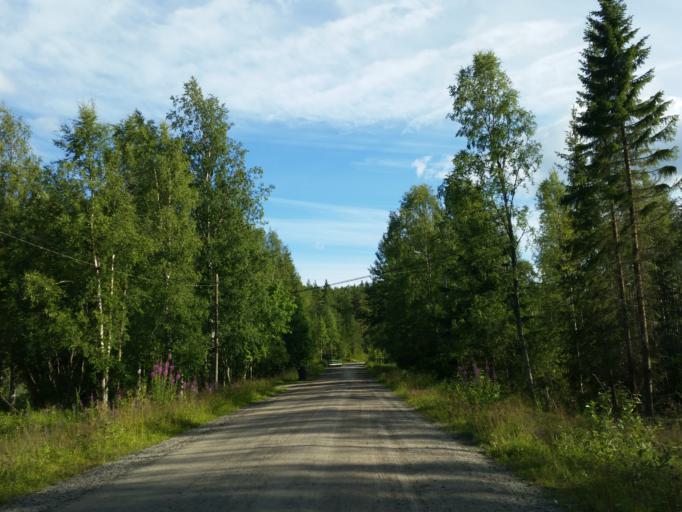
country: SE
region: Vaesterbotten
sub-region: Robertsfors Kommun
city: Robertsfors
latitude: 64.0383
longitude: 20.8508
